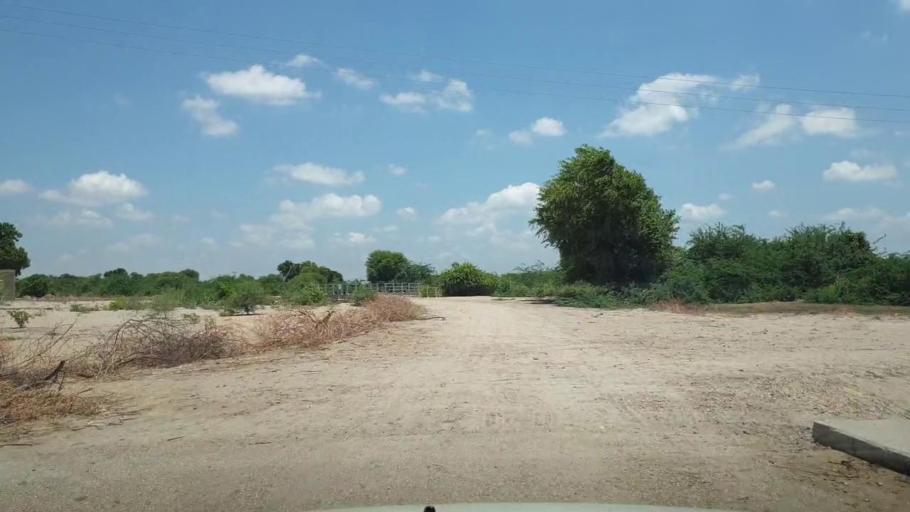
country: PK
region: Sindh
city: Sanghar
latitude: 26.1086
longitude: 69.0163
